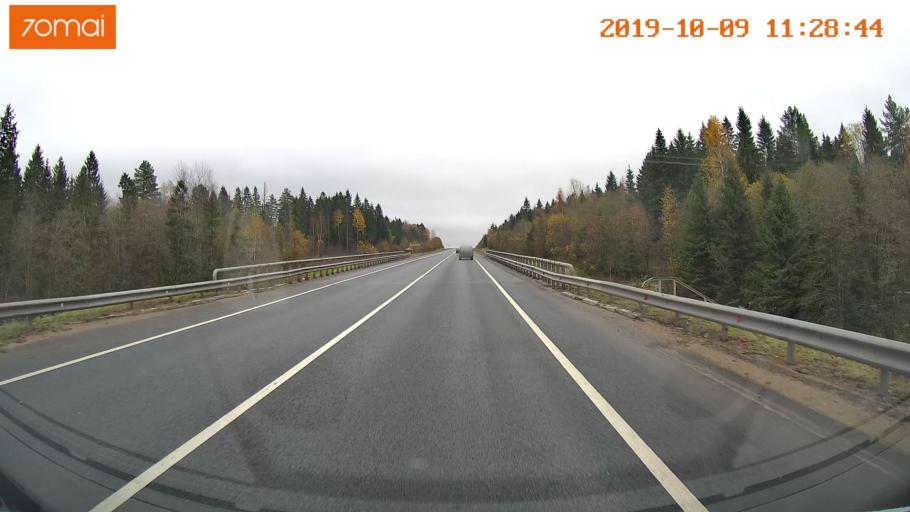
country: RU
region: Vologda
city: Vologda
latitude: 59.0662
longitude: 40.0432
